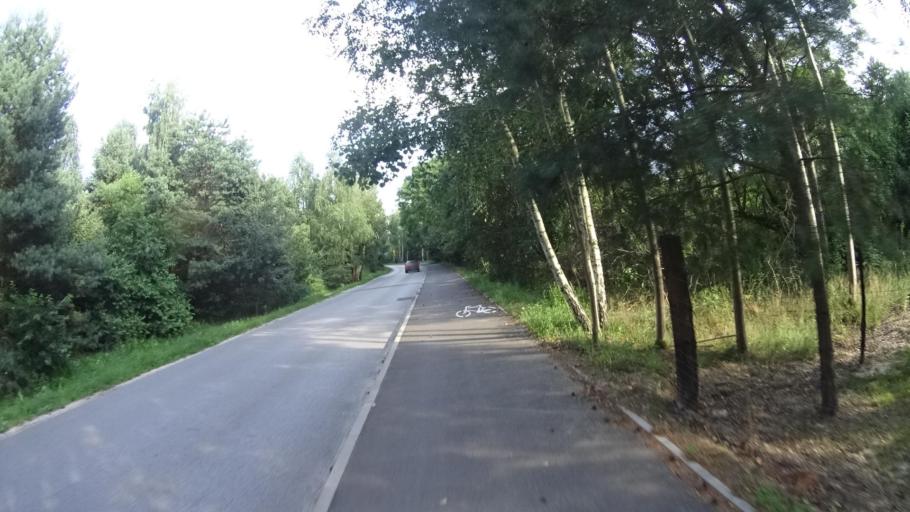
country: PL
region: Masovian Voivodeship
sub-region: Powiat piaseczynski
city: Tarczyn
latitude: 52.0185
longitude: 20.7913
